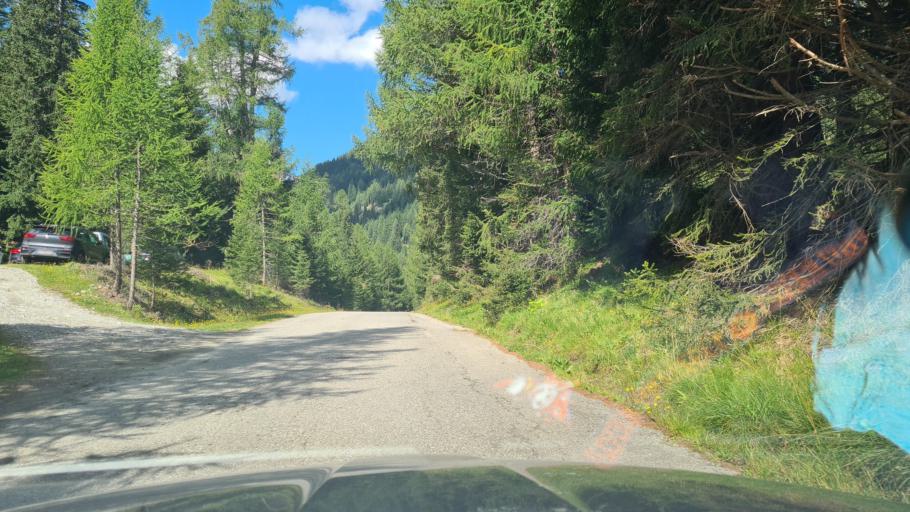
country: AT
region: Salzburg
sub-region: Politischer Bezirk Tamsweg
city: Zederhaus
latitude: 47.1867
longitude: 13.4135
